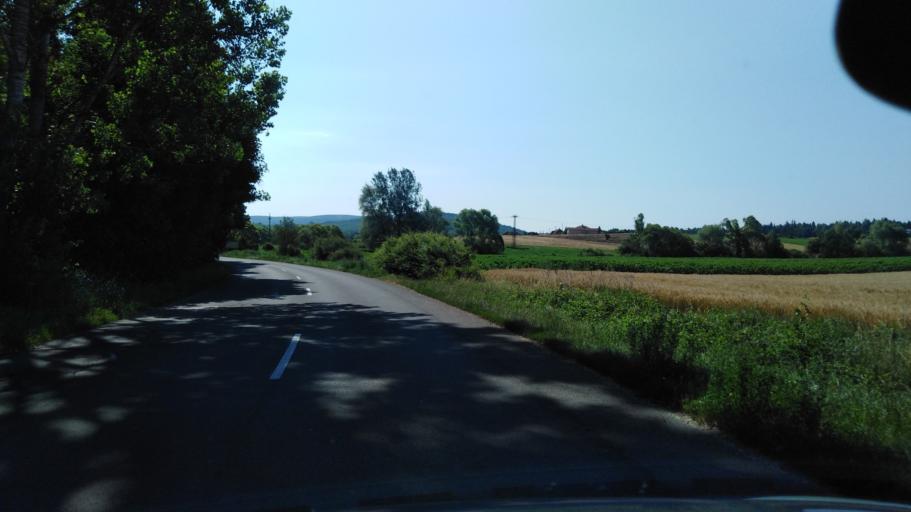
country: HU
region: Nograd
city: Retsag
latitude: 47.9315
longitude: 19.1643
